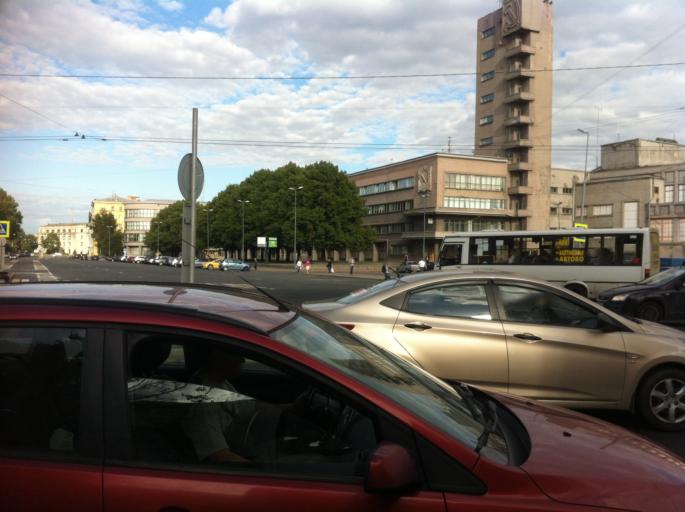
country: RU
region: St.-Petersburg
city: Admiralteisky
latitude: 59.8950
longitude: 30.2753
